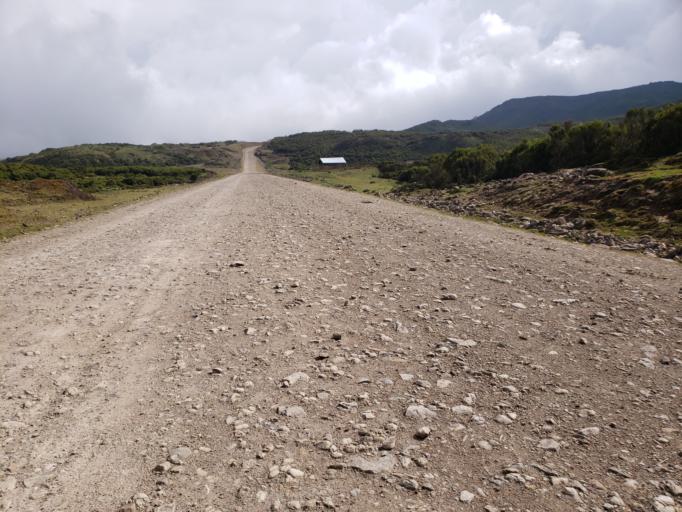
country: ET
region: Oromiya
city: Dodola
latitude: 6.7567
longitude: 39.4286
